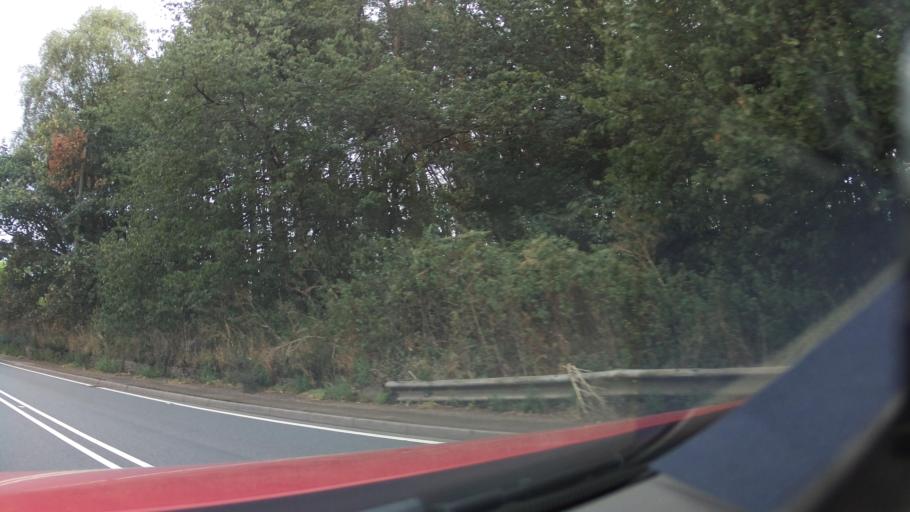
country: GB
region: England
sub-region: Shropshire
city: Woodcote
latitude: 52.7374
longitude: -2.3408
